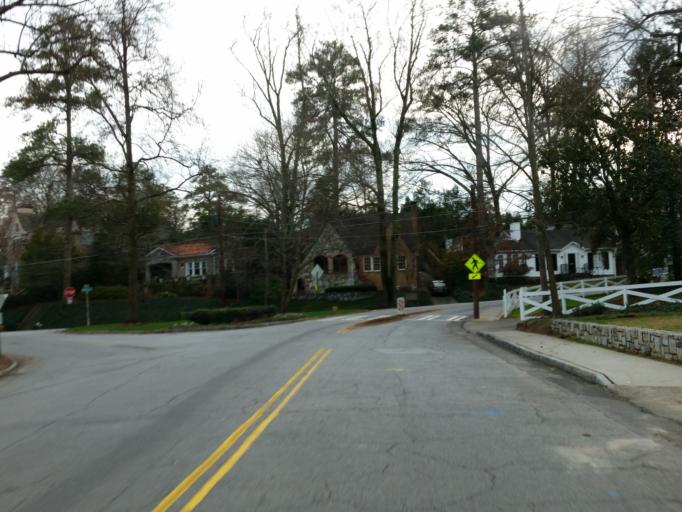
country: US
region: Georgia
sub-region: DeKalb County
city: Druid Hills
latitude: 33.7978
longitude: -84.3765
